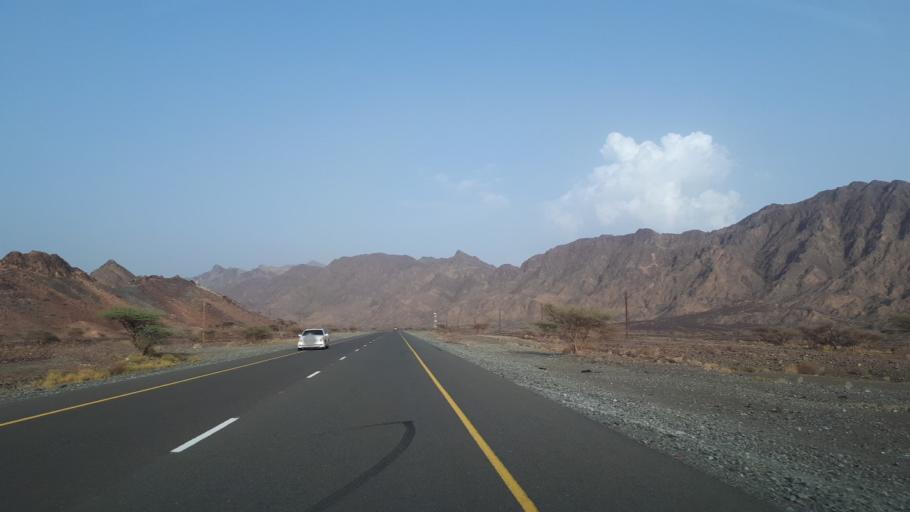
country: OM
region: Az Zahirah
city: Yanqul
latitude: 23.4945
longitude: 56.8607
